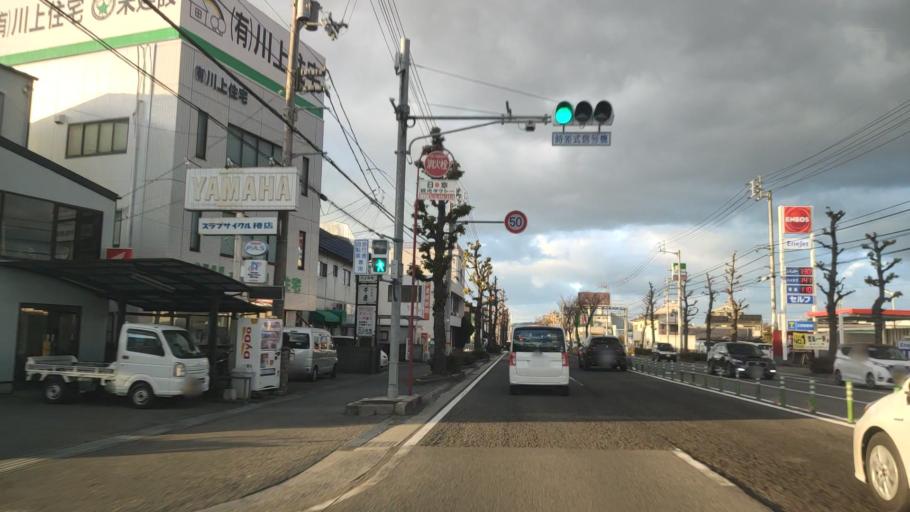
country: JP
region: Ehime
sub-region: Shikoku-chuo Shi
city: Matsuyama
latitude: 33.8068
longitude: 132.7812
